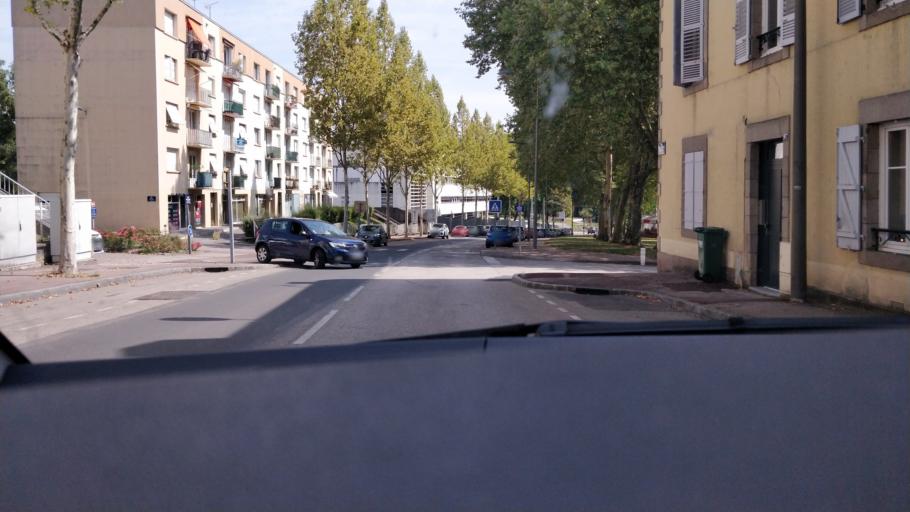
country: FR
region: Limousin
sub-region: Departement de la Haute-Vienne
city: Limoges
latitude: 45.8445
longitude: 1.2505
